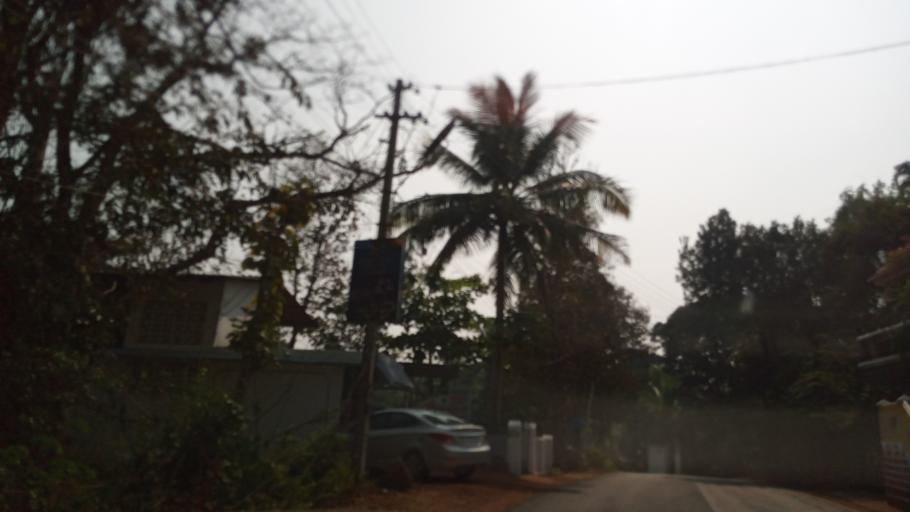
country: IN
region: Goa
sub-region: North Goa
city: Saligao
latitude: 15.5435
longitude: 73.8096
